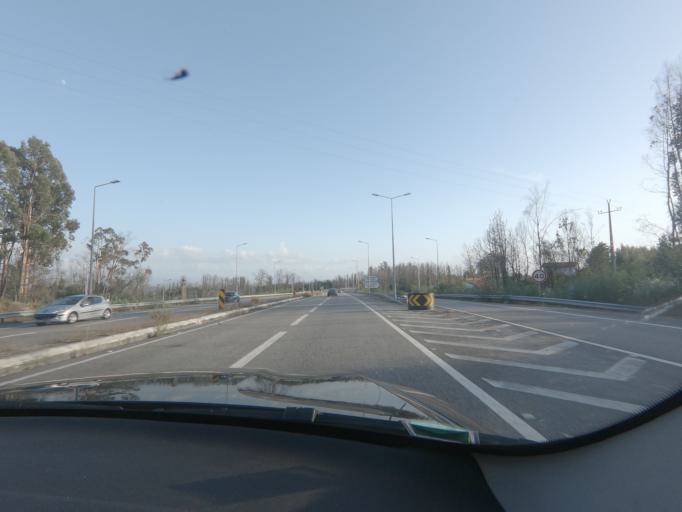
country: PT
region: Viseu
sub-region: Santa Comba Dao
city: Santa Comba Dao
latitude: 40.4388
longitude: -8.1095
